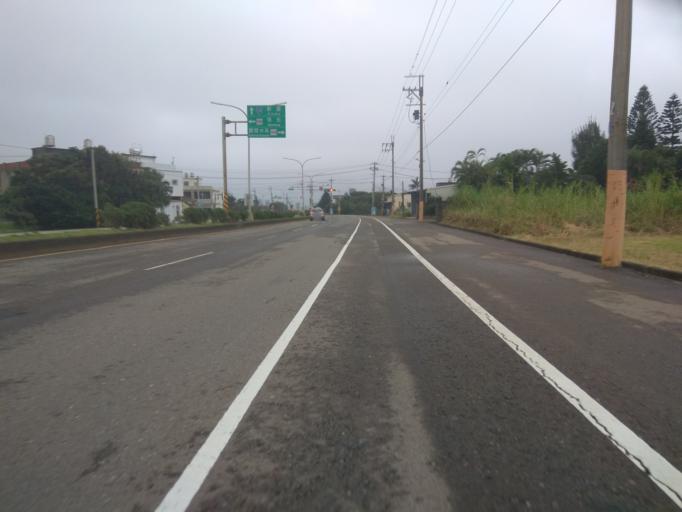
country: TW
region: Taiwan
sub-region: Hsinchu
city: Zhubei
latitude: 25.0308
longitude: 121.0763
